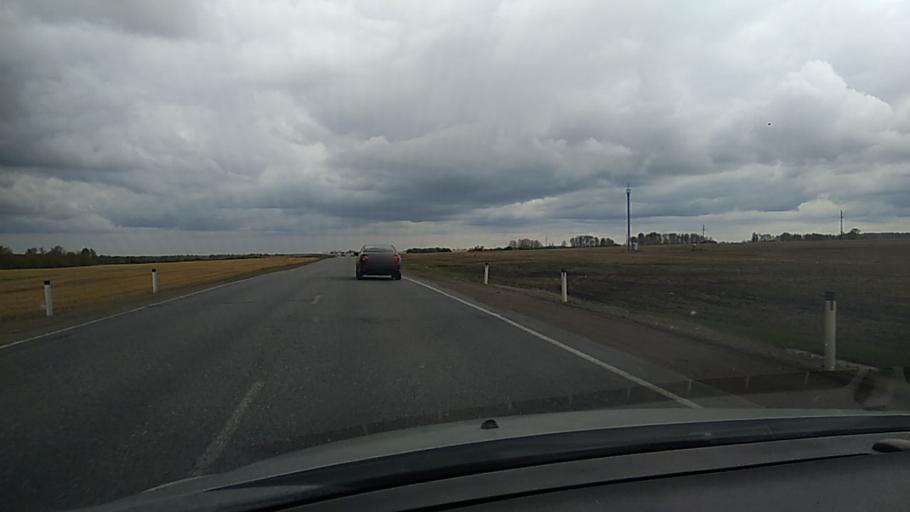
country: RU
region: Kurgan
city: Dalmatovo
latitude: 56.2895
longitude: 62.7932
